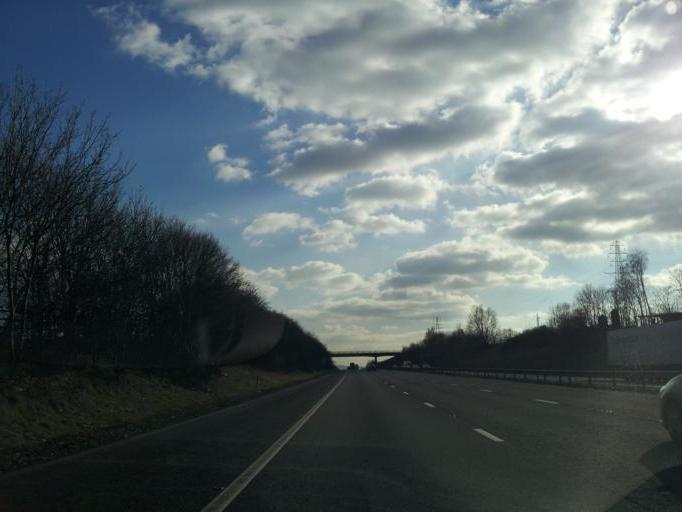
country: GB
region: England
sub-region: Somerset
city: North Petherton
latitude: 51.0705
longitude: -3.0145
